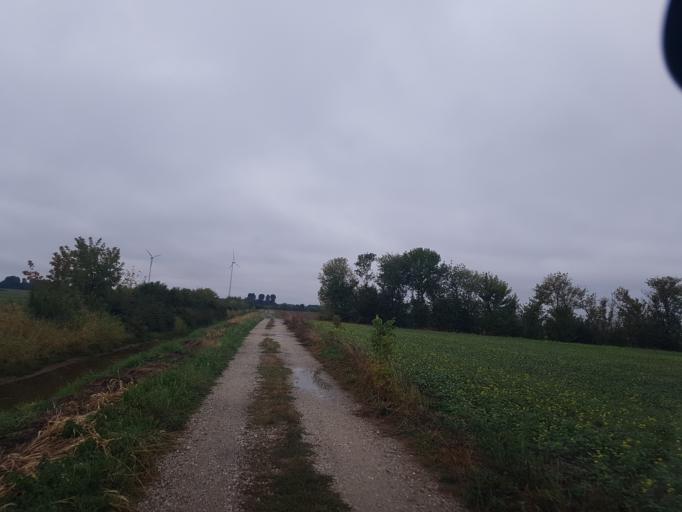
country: DE
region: Brandenburg
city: Merzdorf
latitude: 51.4190
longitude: 13.5213
